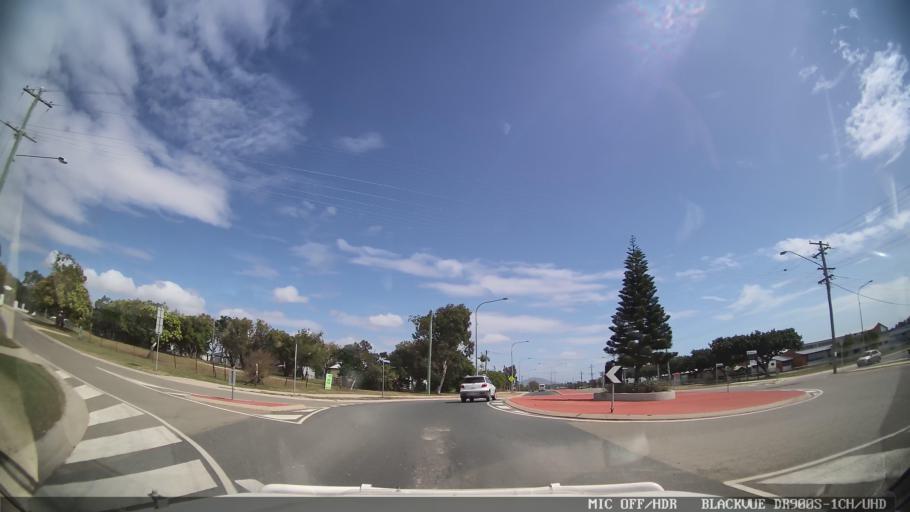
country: AU
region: Queensland
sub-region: Whitsunday
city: Bowen
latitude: -20.0006
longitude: 148.2357
